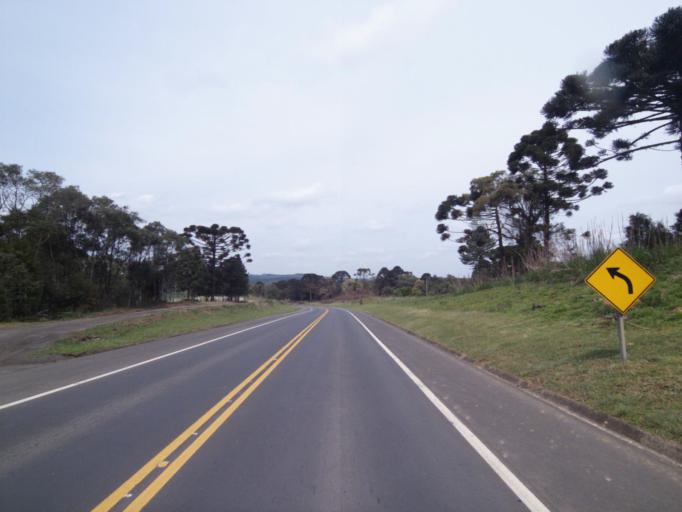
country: BR
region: Parana
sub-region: Irati
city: Irati
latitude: -25.4658
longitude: -50.5372
